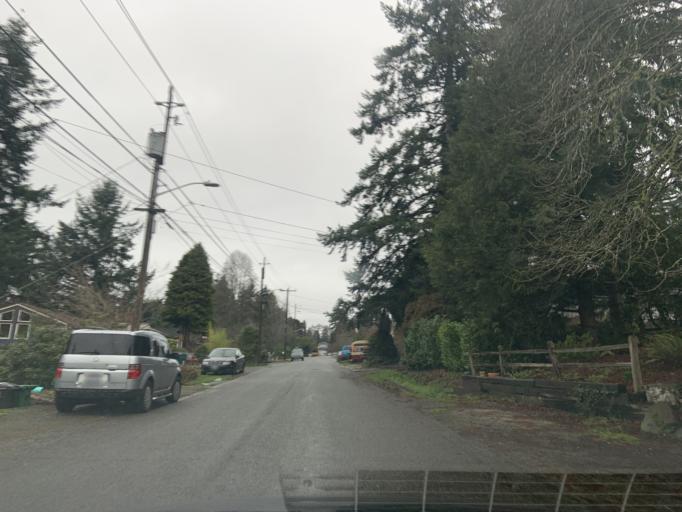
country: US
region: Washington
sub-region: King County
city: Lake Forest Park
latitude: 47.7107
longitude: -122.2881
